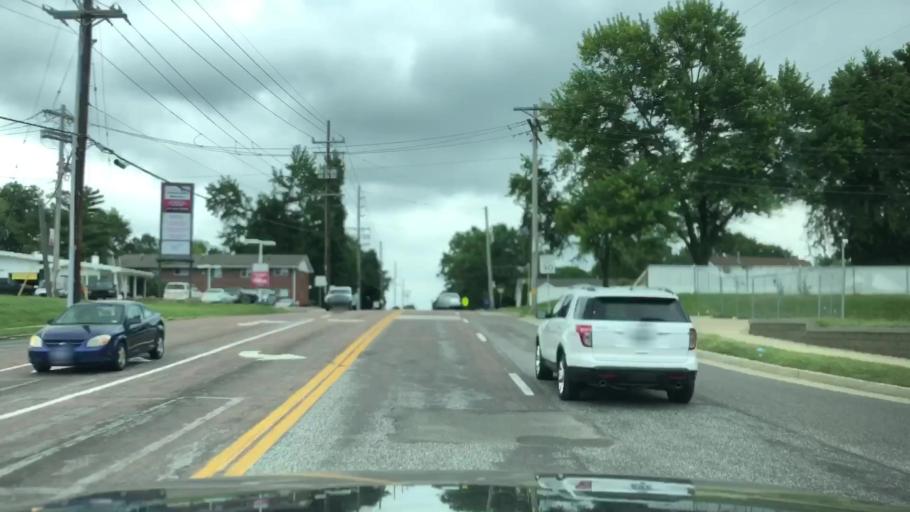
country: US
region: Missouri
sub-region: Saint Louis County
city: Hazelwood
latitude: 38.8086
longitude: -90.3583
